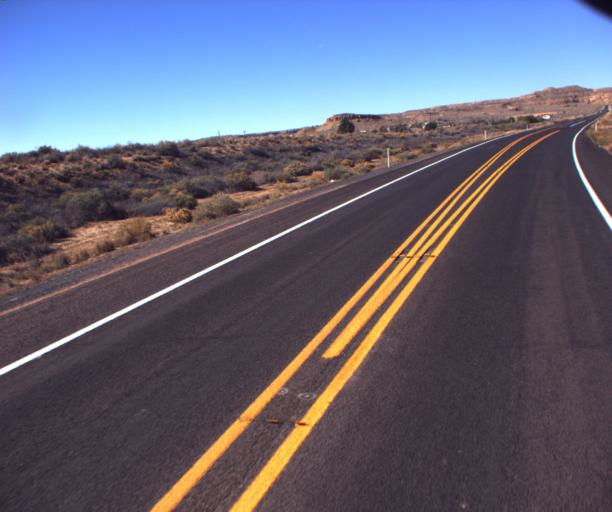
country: US
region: Arizona
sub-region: Navajo County
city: First Mesa
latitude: 35.8743
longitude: -110.6045
